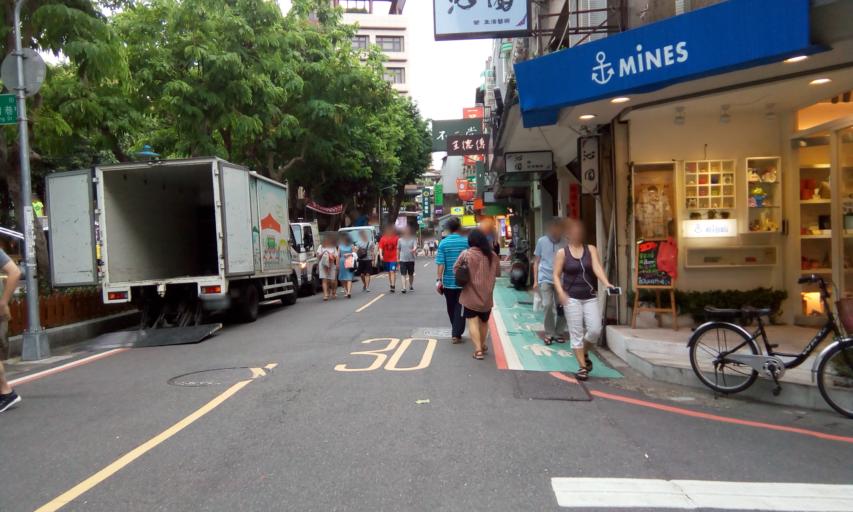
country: TW
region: Taipei
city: Taipei
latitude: 25.0320
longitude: 121.5297
